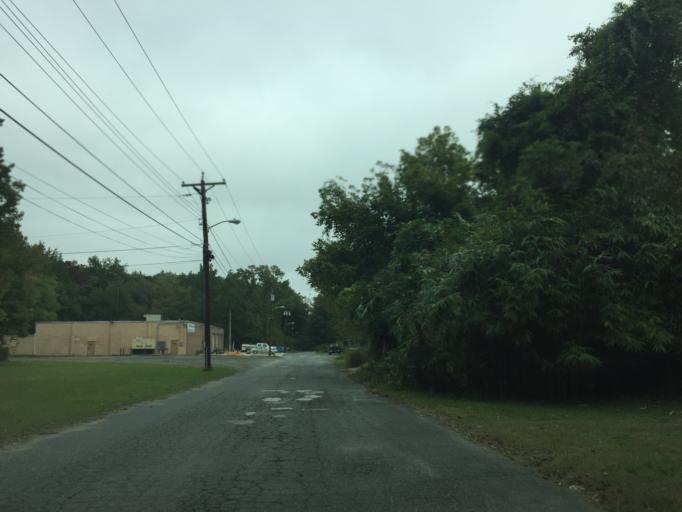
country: US
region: Maryland
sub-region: Baltimore County
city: Middle River
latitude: 39.3345
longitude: -76.4350
